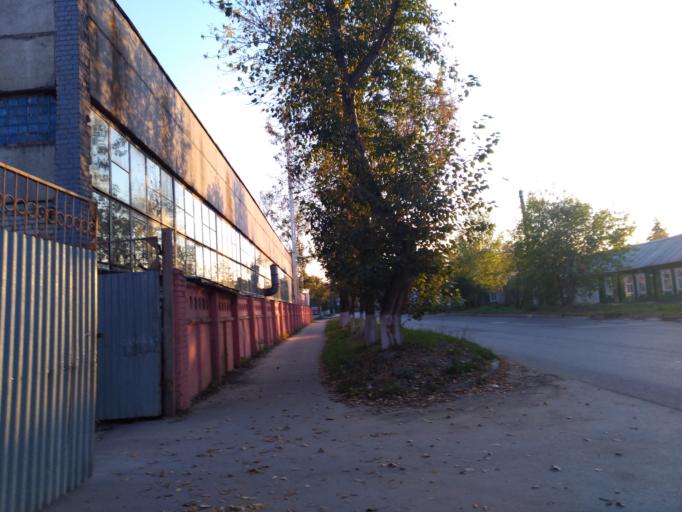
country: RU
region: Kaluga
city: Kaluga
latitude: 54.5204
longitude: 36.2817
